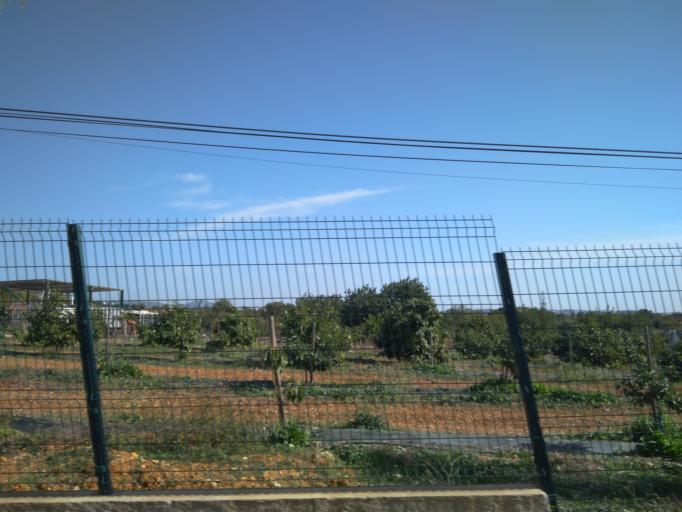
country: PT
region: Faro
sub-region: Faro
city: Santa Barbara de Nexe
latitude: 37.0821
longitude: -7.9586
